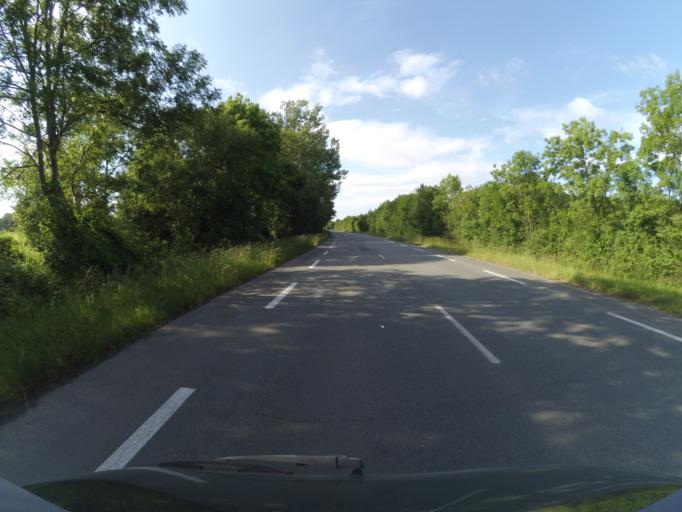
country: FR
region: Poitou-Charentes
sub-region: Departement de la Charente-Maritime
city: Saint-Agnant
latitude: 45.8176
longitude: -0.9310
